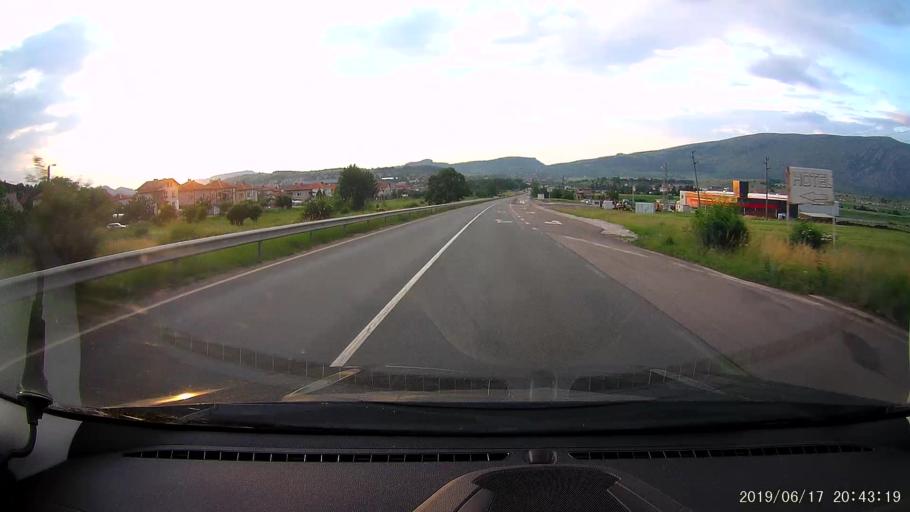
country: BG
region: Sofiya
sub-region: Obshtina Dragoman
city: Dragoman
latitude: 42.9139
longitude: 22.9411
